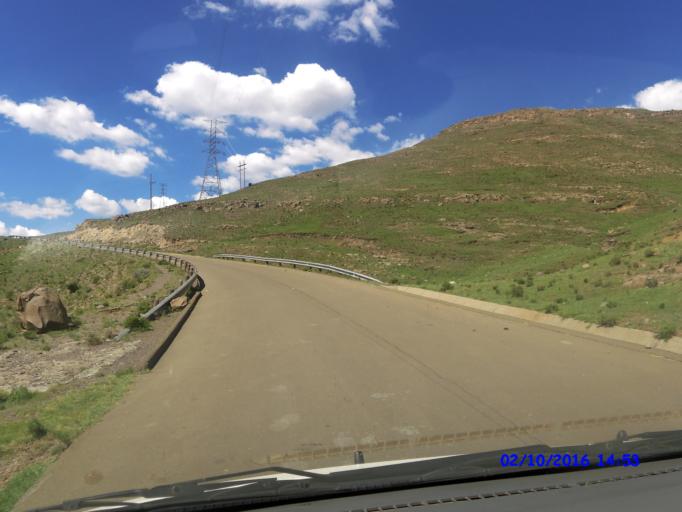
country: LS
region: Maseru
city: Nako
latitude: -29.4814
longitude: 28.0782
